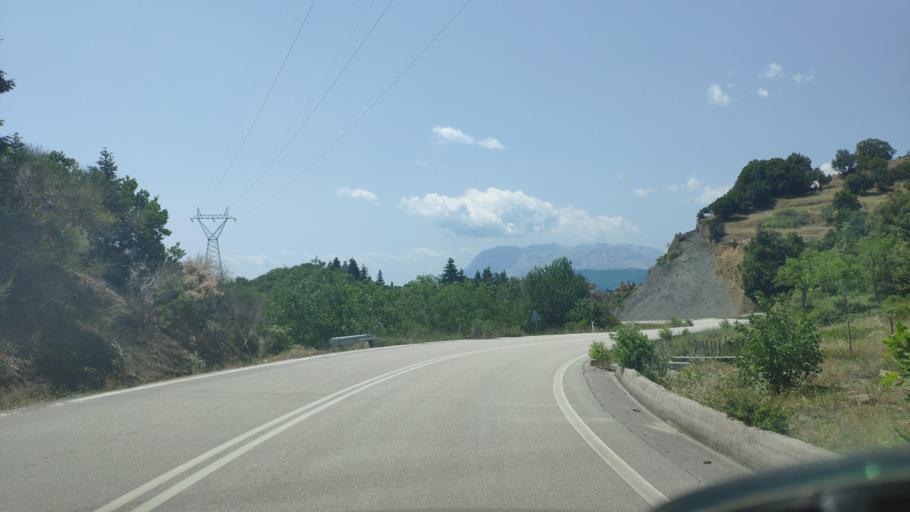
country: GR
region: Epirus
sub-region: Nomos Artas
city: Ano Kalentini
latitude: 39.2824
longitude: 21.3204
